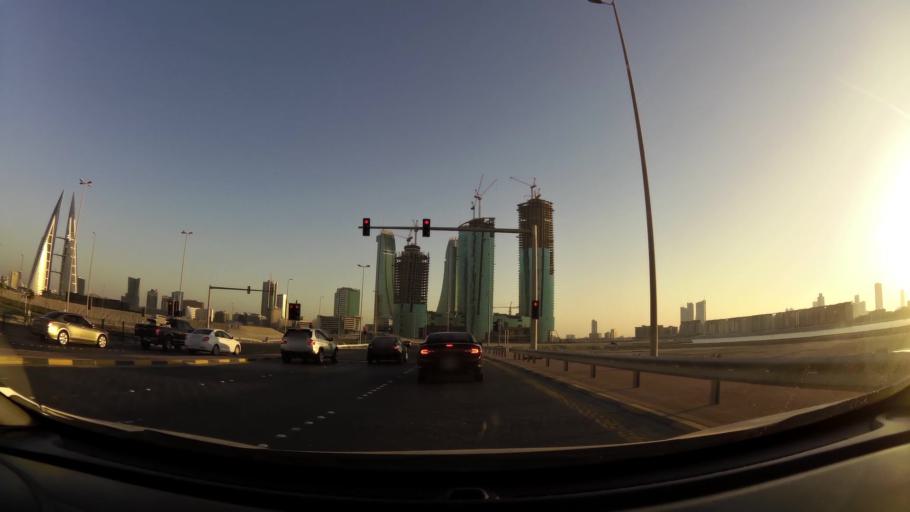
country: BH
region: Manama
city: Manama
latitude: 26.2462
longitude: 50.5744
